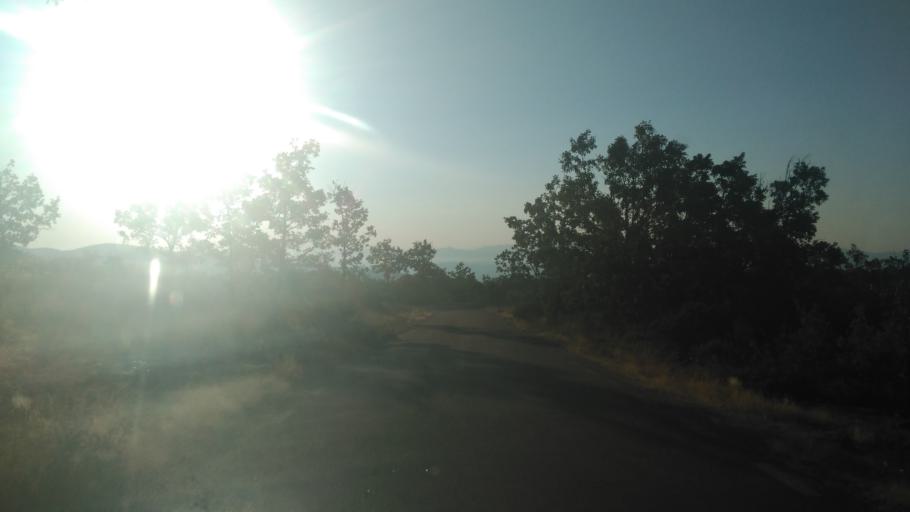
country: ES
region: Castille and Leon
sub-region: Provincia de Salamanca
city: Nava de Francia
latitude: 40.5225
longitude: -6.1068
